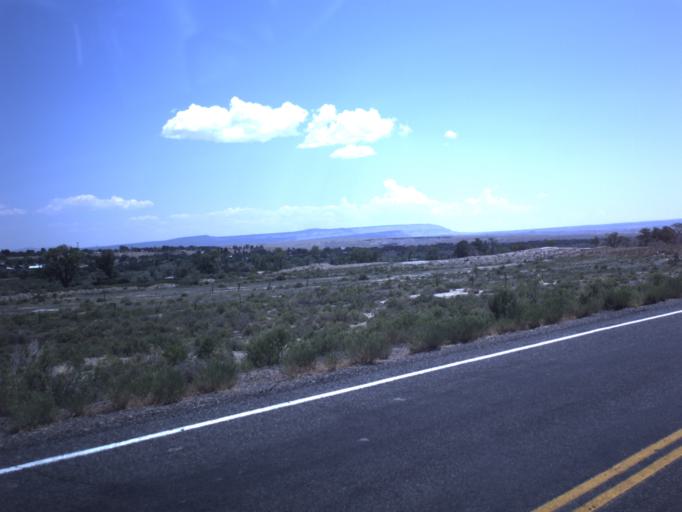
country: US
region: Utah
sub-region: Emery County
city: Orangeville
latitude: 39.2114
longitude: -111.0495
